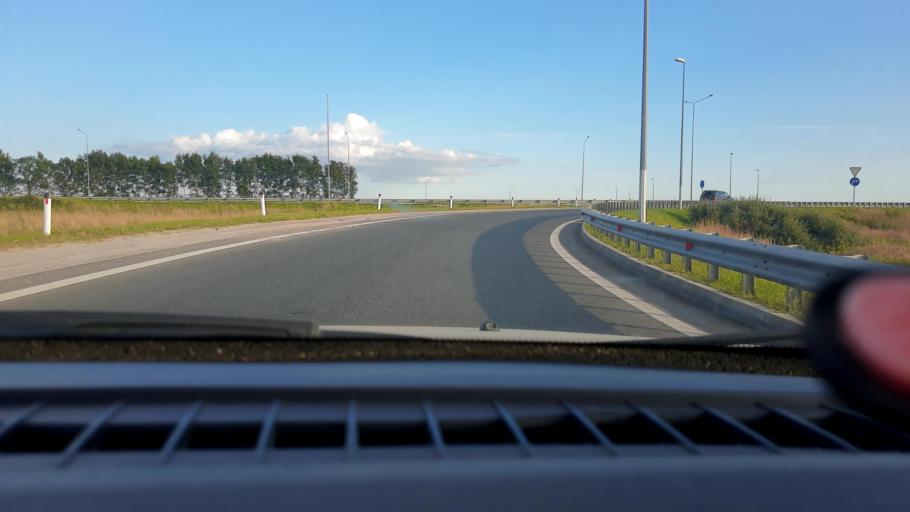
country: RU
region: Nizjnij Novgorod
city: Burevestnik
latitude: 56.1187
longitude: 43.9189
